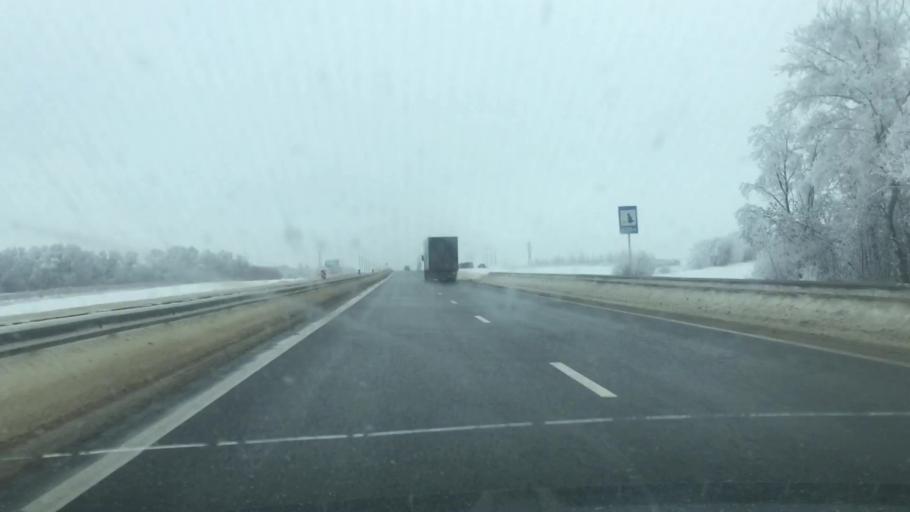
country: RU
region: Lipetsk
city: Stanovoye
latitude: 52.8918
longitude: 38.2387
